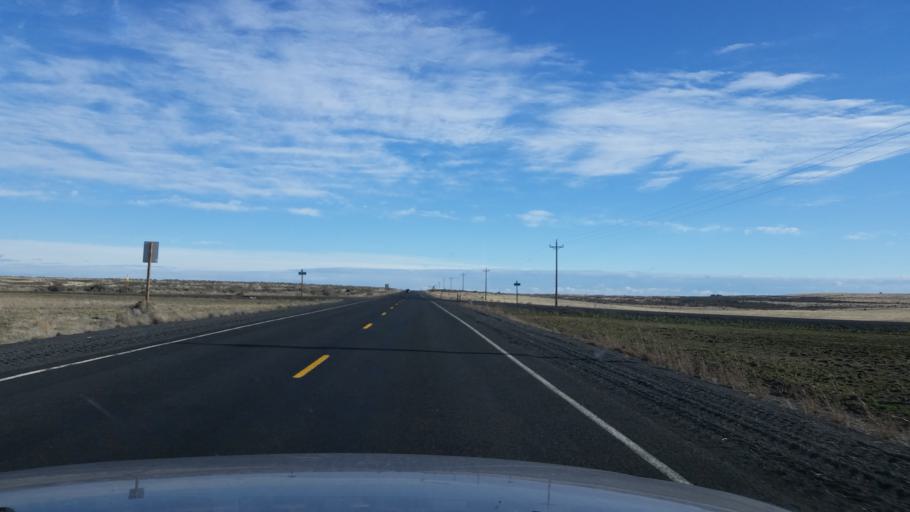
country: US
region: Washington
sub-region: Grant County
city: Warden
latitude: 47.3156
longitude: -118.8103
